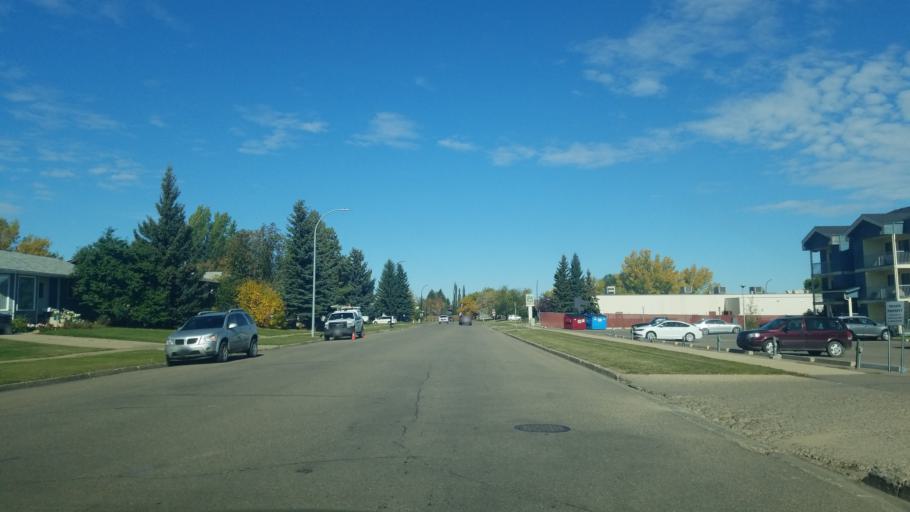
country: CA
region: Saskatchewan
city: Lloydminster
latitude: 53.2719
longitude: -110.0119
